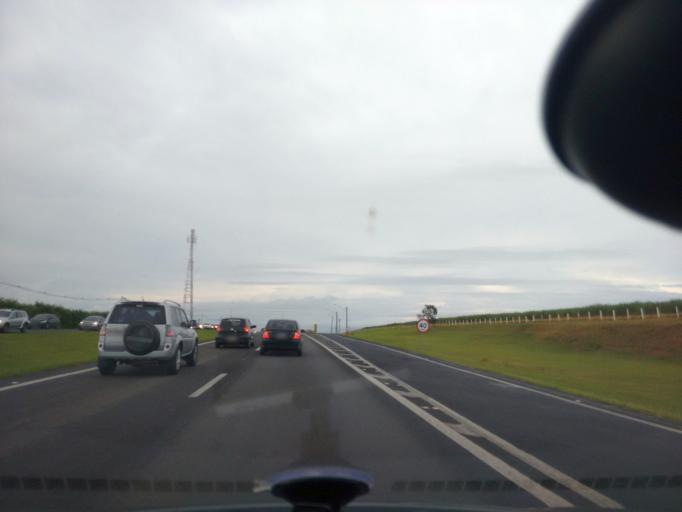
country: BR
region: Sao Paulo
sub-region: Itirapina
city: Itirapina
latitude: -22.1924
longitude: -47.7767
